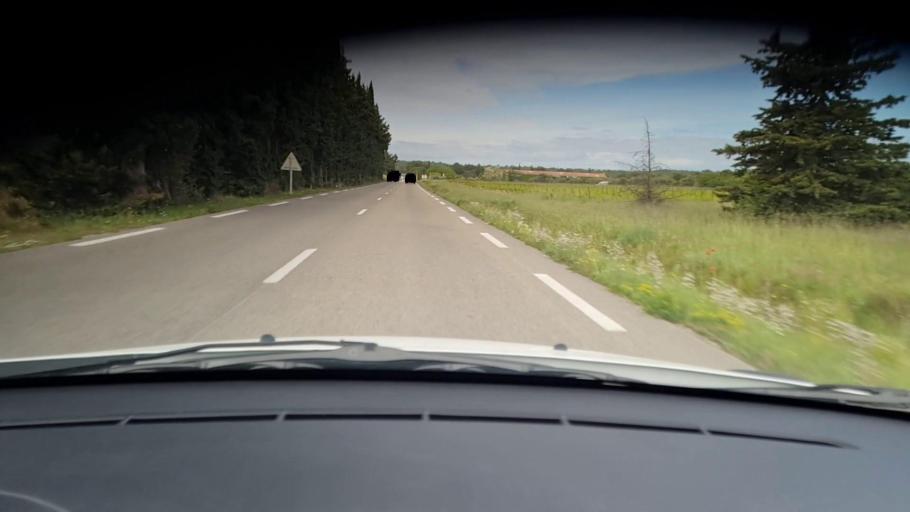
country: FR
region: Languedoc-Roussillon
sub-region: Departement du Gard
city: Castillon-du-Gard
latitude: 43.9551
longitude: 4.5609
